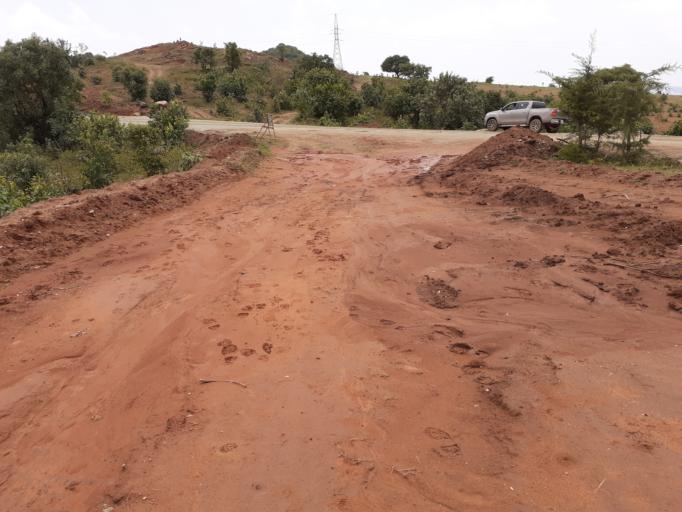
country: ET
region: Oromiya
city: Gimbi
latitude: 9.3331
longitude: 35.6983
